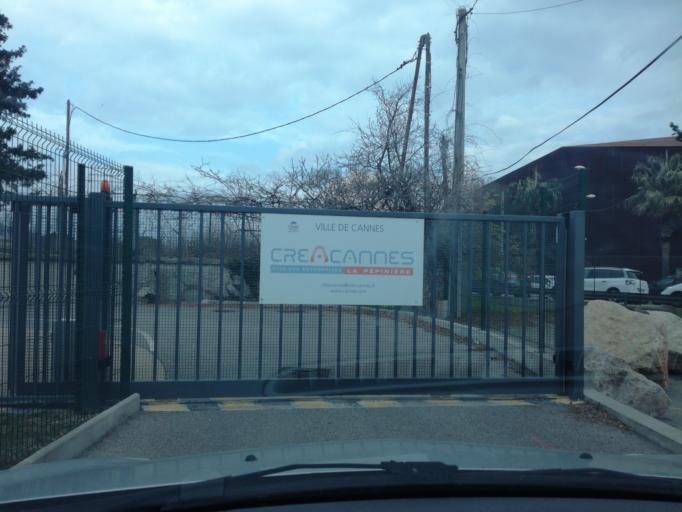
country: FR
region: Provence-Alpes-Cote d'Azur
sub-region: Departement des Alpes-Maritimes
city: Mandelieu-la-Napoule
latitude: 43.5513
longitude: 6.9609
